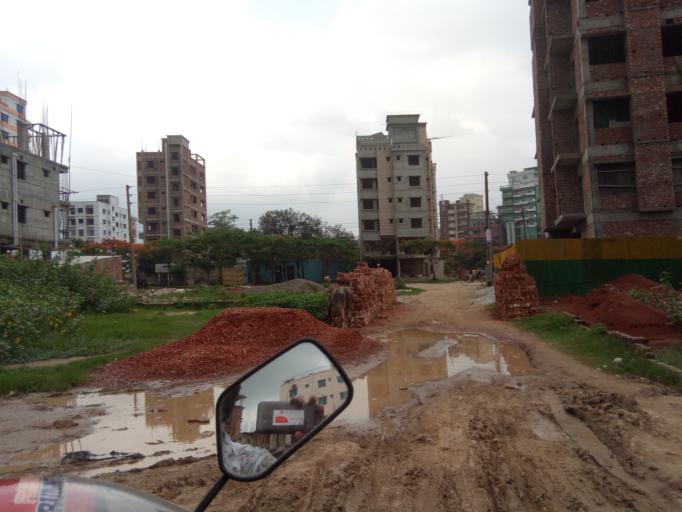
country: BD
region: Dhaka
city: Paltan
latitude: 23.7645
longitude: 90.4346
